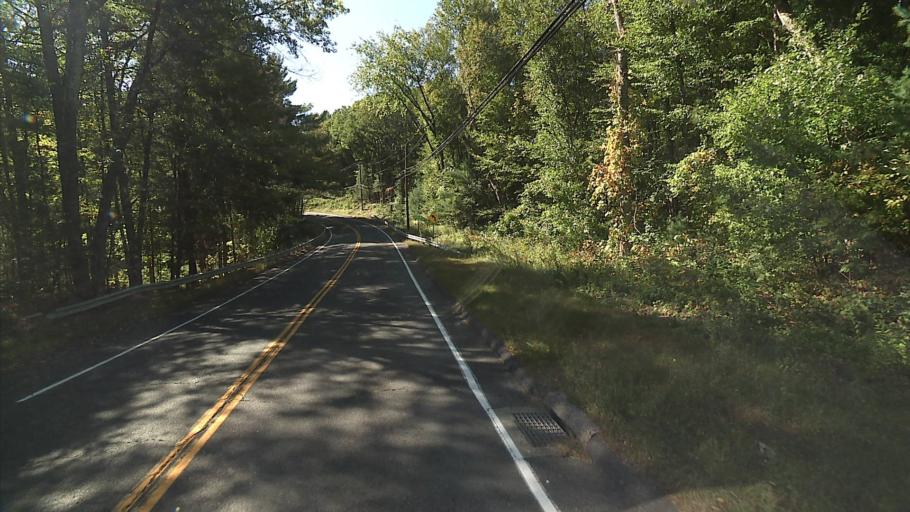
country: US
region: Connecticut
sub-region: Hartford County
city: Bristol
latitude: 41.7257
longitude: -72.9498
